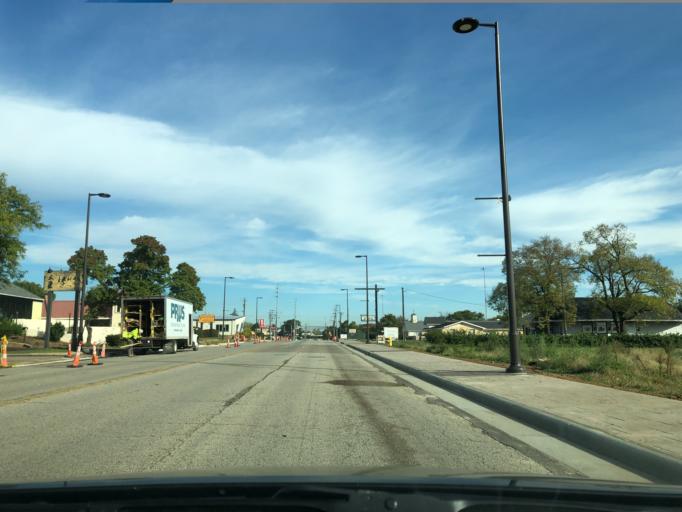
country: US
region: Ohio
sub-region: Hamilton County
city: Glendale
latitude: 39.2822
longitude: -84.4432
